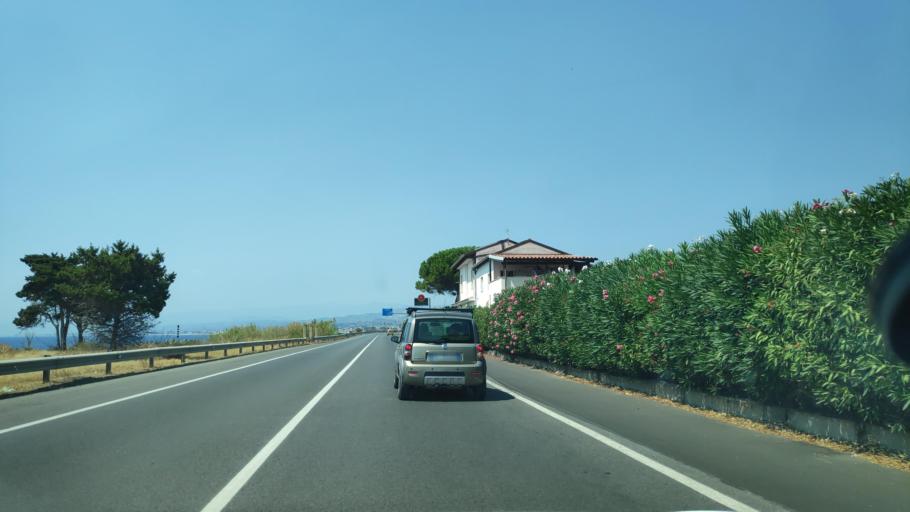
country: IT
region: Calabria
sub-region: Provincia di Reggio Calabria
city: Marina di Gioiosa Ionica
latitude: 38.3069
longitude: 16.3592
